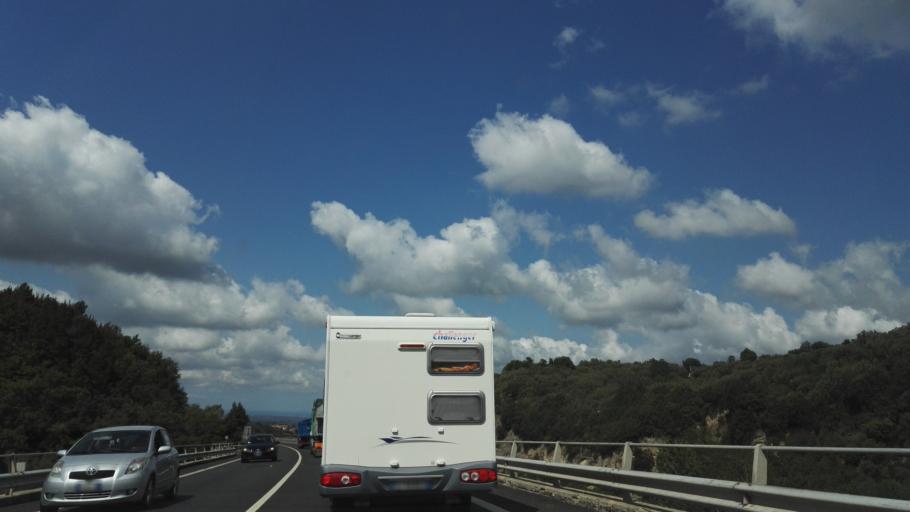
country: IT
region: Calabria
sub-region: Provincia di Reggio Calabria
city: Anoia Superiore
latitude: 38.4178
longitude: 16.1191
